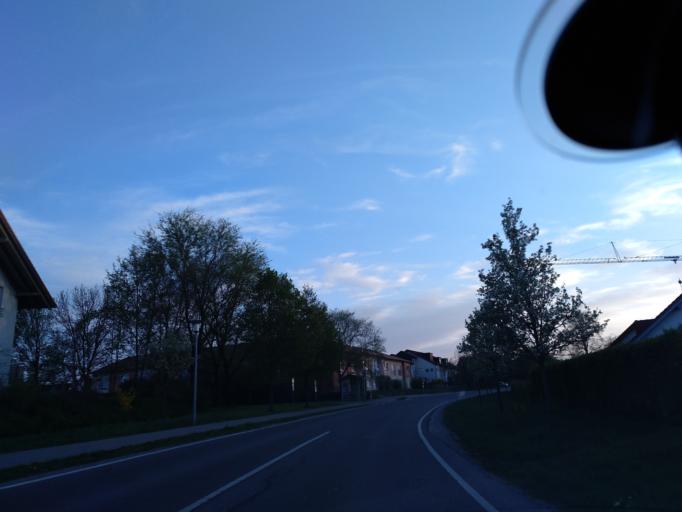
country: DE
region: Baden-Wuerttemberg
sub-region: Regierungsbezirk Stuttgart
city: Satteldorf
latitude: 49.1684
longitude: 10.0862
